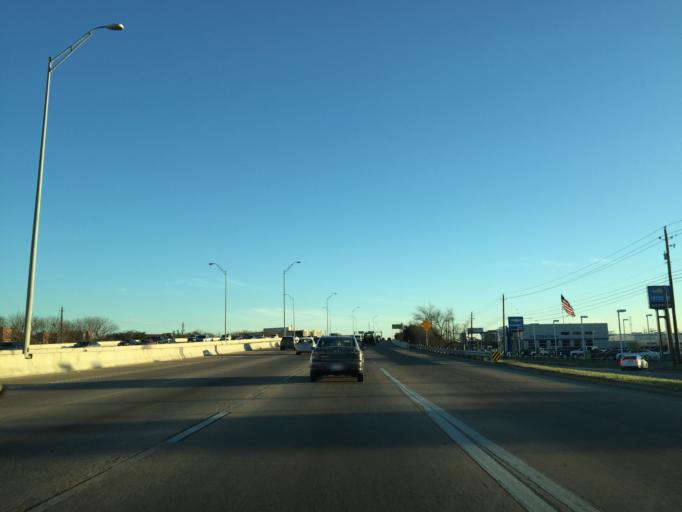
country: US
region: Texas
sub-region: Williamson County
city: Jollyville
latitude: 30.4117
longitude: -97.7457
